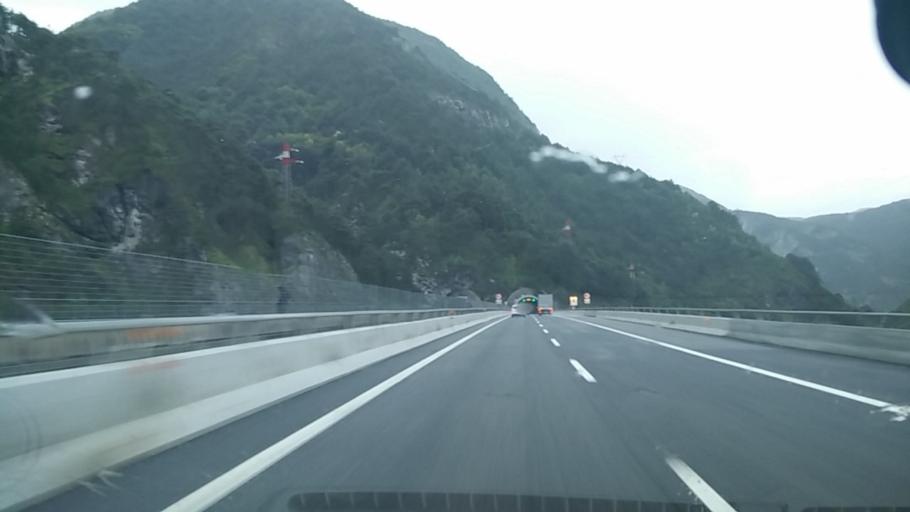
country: IT
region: Friuli Venezia Giulia
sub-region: Provincia di Udine
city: Chiusaforte
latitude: 46.4217
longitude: 13.3196
